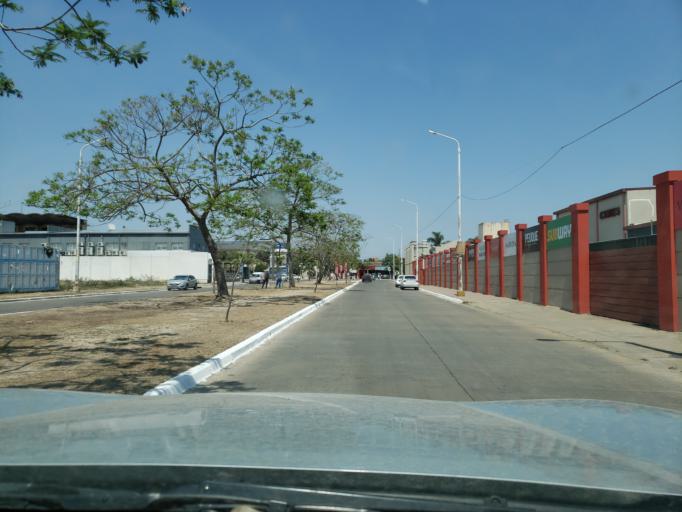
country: AR
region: Corrientes
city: Corrientes
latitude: -27.4714
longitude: -58.8059
